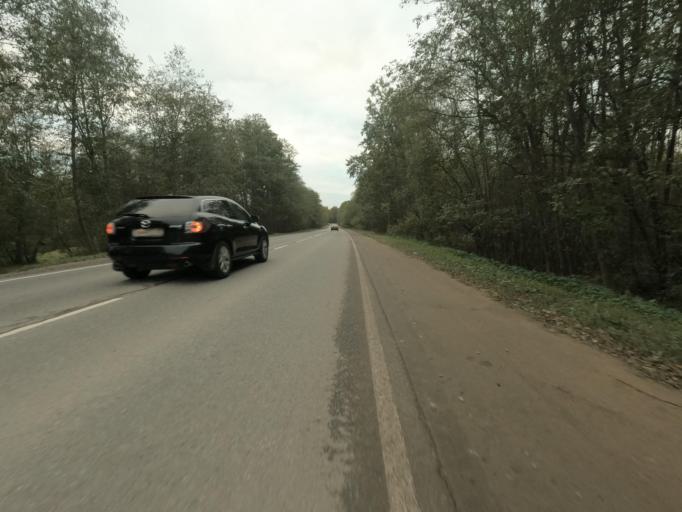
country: RU
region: Leningrad
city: Pavlovo
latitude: 59.7946
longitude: 30.9529
